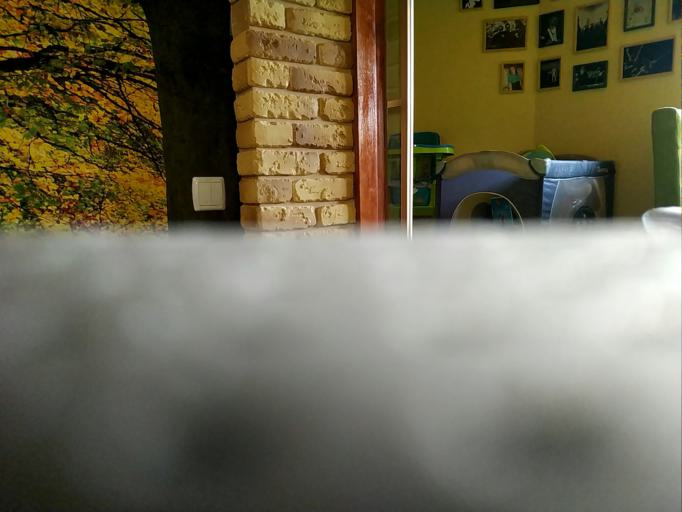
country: RU
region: Kaluga
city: Seredeyskiy
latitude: 54.0050
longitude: 35.3155
